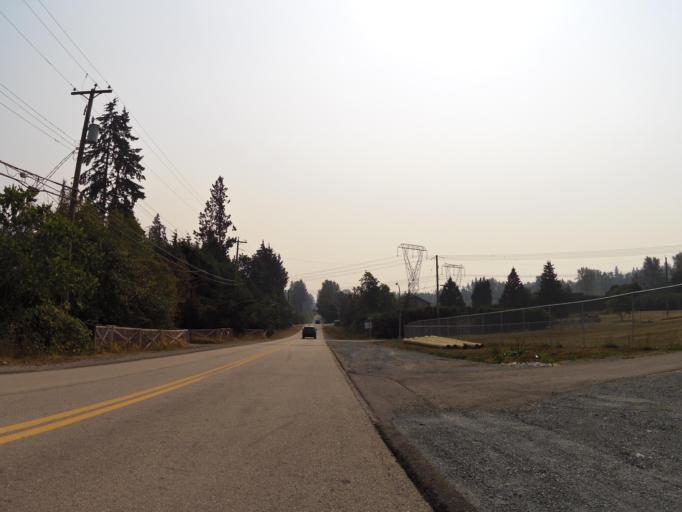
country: US
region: Washington
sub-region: Whatcom County
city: Blaine
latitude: 49.0299
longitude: -122.7572
